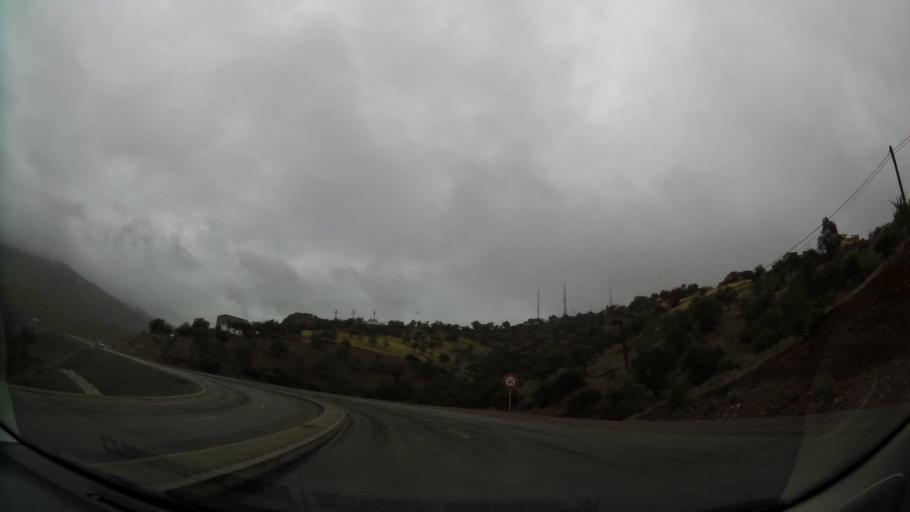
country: MA
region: Taza-Al Hoceima-Taounate
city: Imzourene
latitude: 35.0325
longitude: -3.8228
